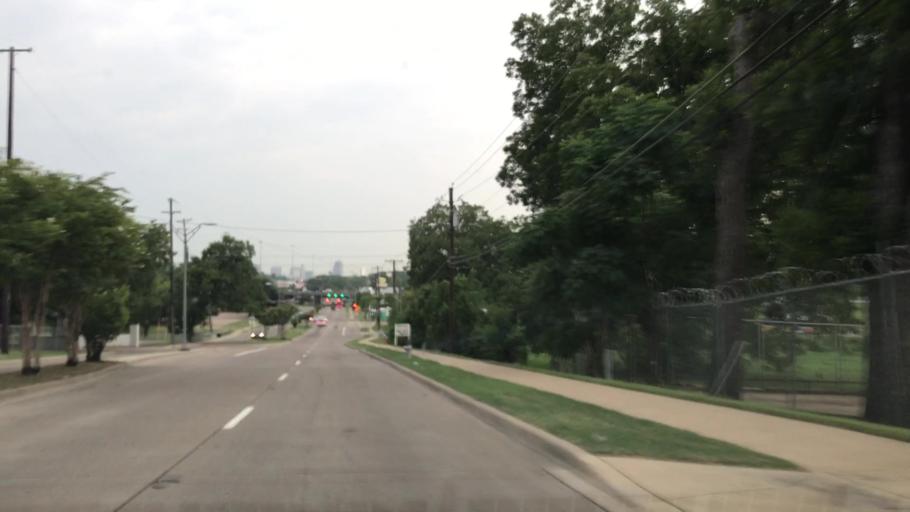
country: US
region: Texas
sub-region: Dallas County
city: Highland Park
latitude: 32.7934
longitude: -96.7220
